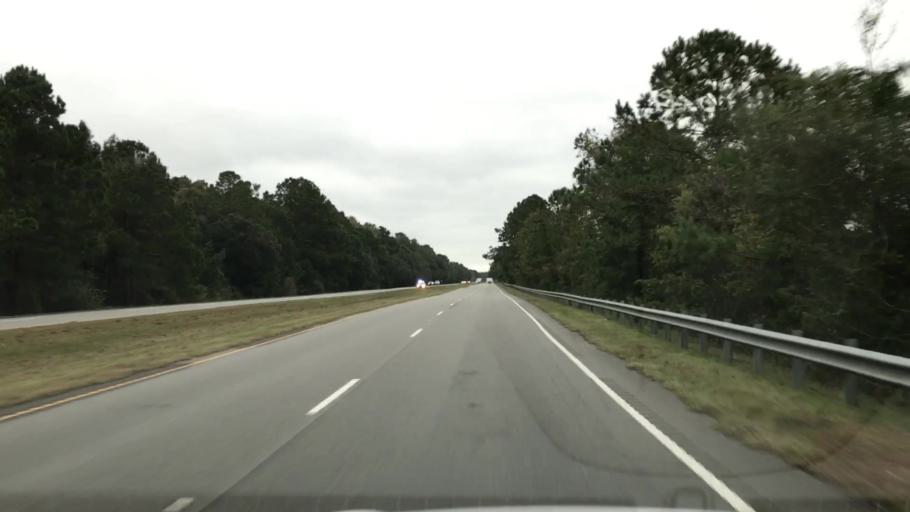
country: US
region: South Carolina
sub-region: Georgetown County
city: Georgetown
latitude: 33.1970
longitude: -79.3945
